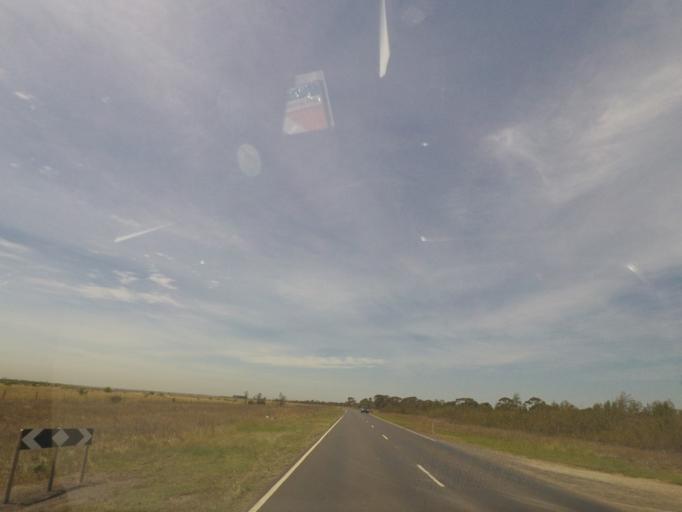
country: AU
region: Victoria
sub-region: Wyndham
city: Wyndham Vale
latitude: -37.8319
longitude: 144.5430
